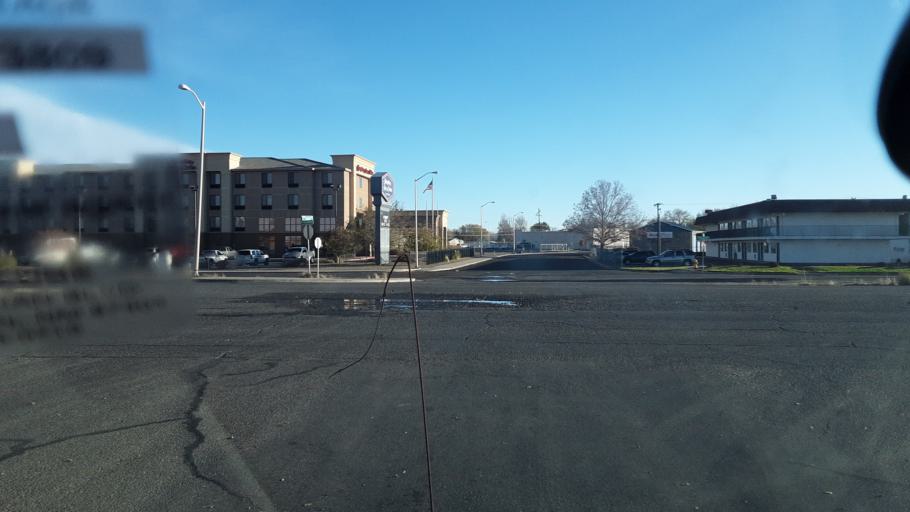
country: US
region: New Mexico
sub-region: San Juan County
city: Farmington
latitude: 36.7248
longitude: -108.1888
